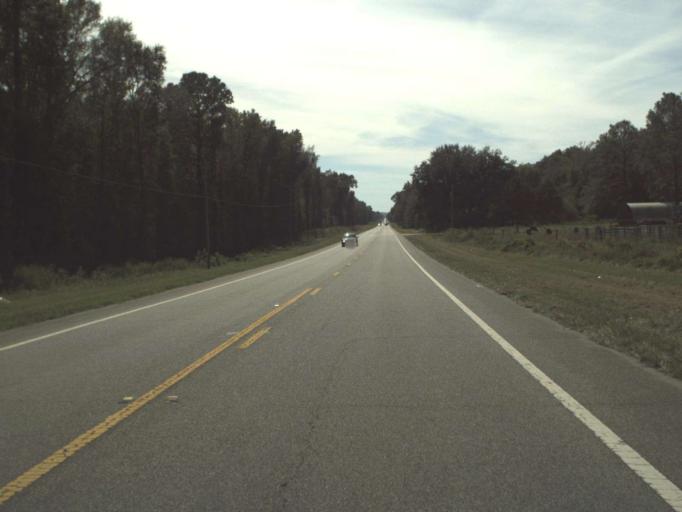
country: US
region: Florida
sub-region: Washington County
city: Chipley
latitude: 30.7117
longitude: -85.5581
